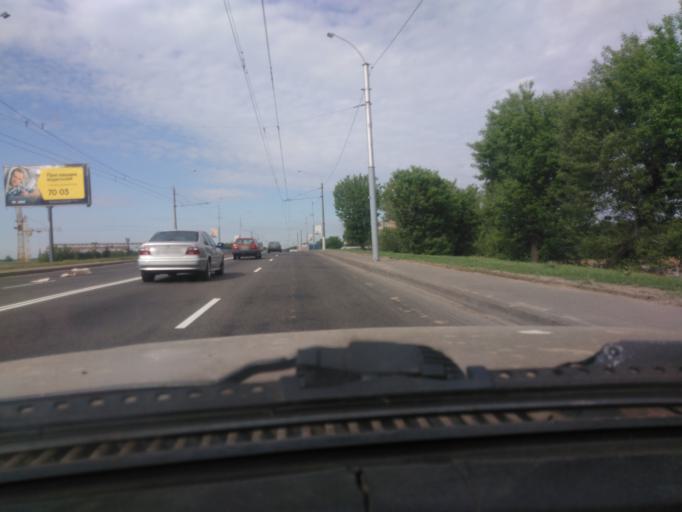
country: BY
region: Mogilev
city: Buynichy
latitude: 53.8910
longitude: 30.2934
